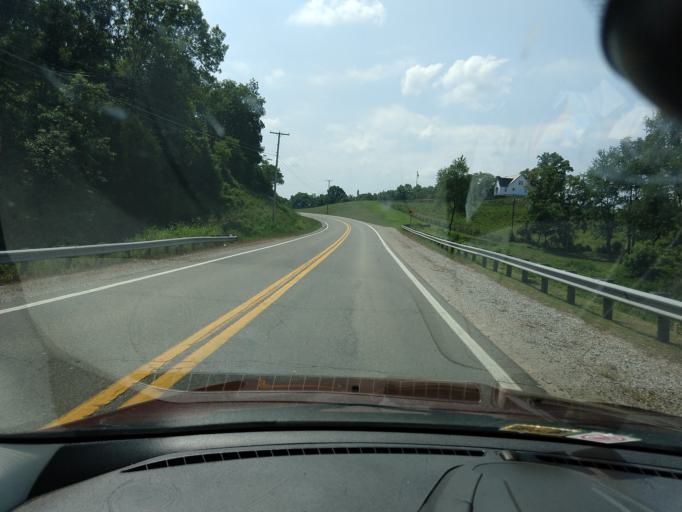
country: US
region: West Virginia
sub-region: Jackson County
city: Ravenswood
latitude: 38.8814
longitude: -81.8351
